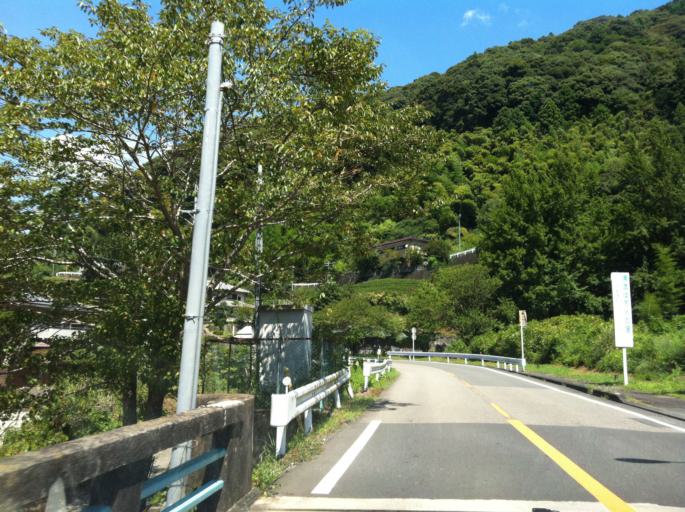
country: JP
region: Shizuoka
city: Shizuoka-shi
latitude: 35.0200
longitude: 138.2610
